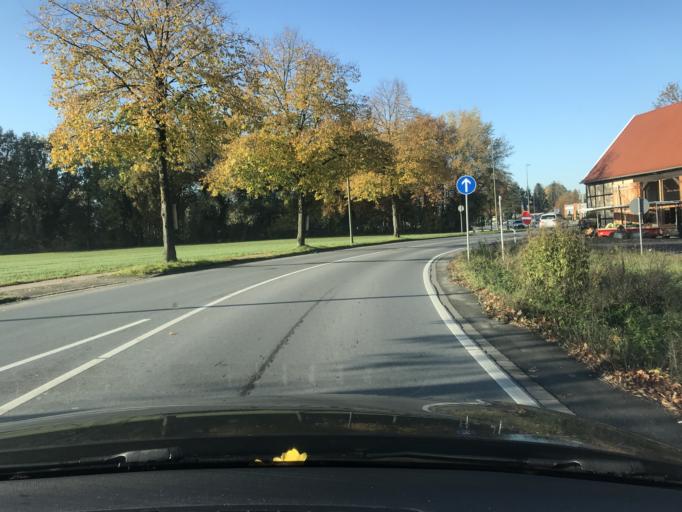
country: DE
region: North Rhine-Westphalia
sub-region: Regierungsbezirk Arnsberg
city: Hamm
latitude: 51.6543
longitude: 7.8416
